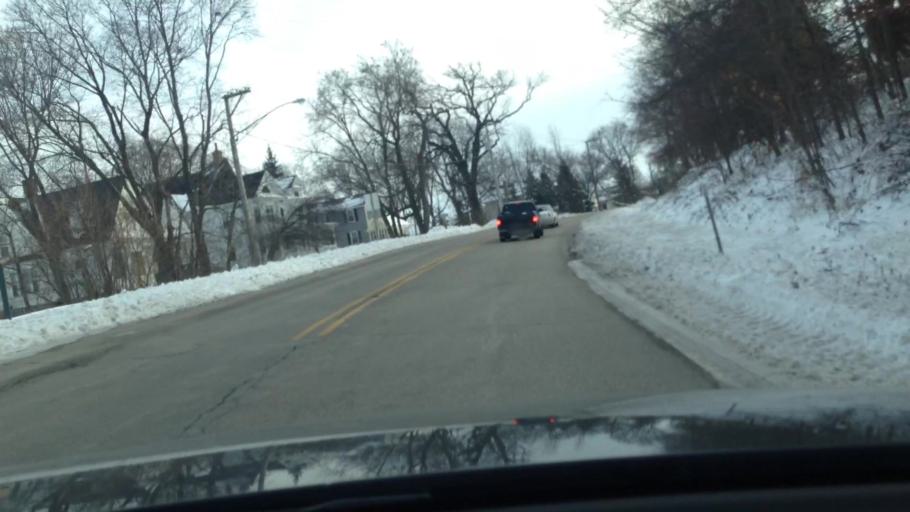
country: US
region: Illinois
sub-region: McHenry County
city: Hebron
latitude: 42.4755
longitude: -88.4330
